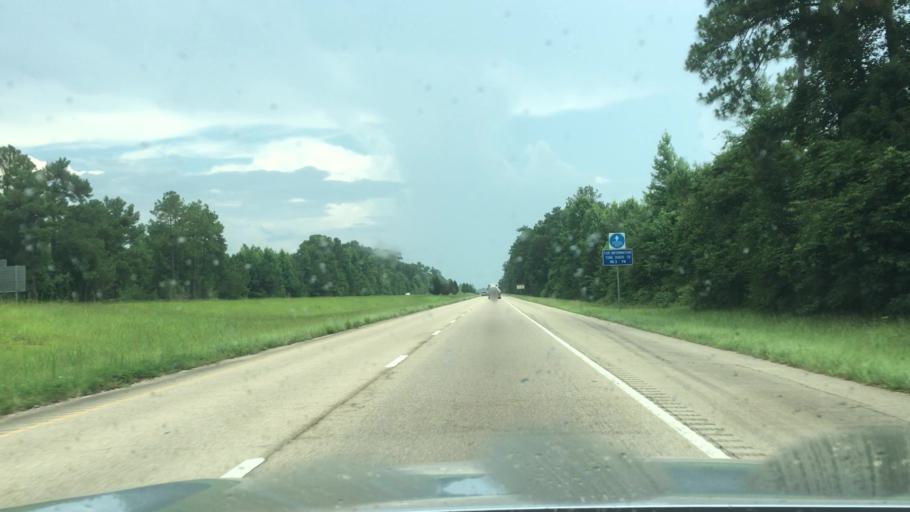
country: US
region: Mississippi
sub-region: Lamar County
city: Lumberton
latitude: 31.0161
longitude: -89.4108
